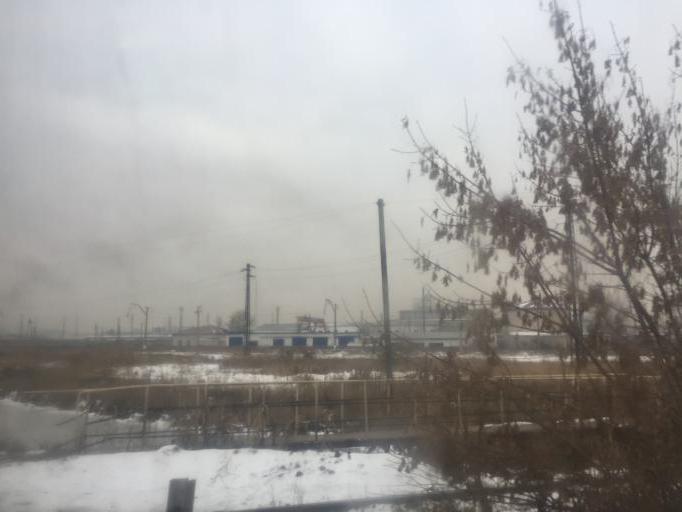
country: KZ
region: Astana Qalasy
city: Astana
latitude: 51.1990
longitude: 71.4112
